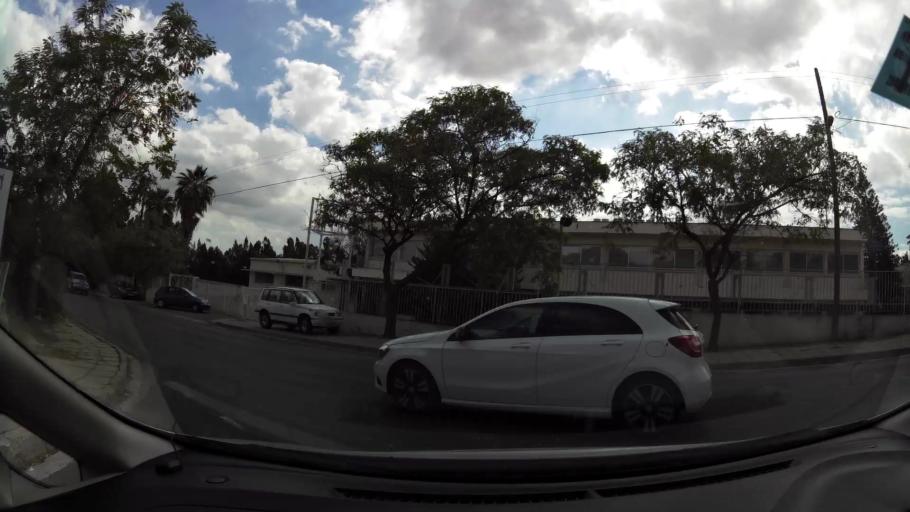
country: CY
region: Lefkosia
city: Nicosia
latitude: 35.1792
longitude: 33.3902
